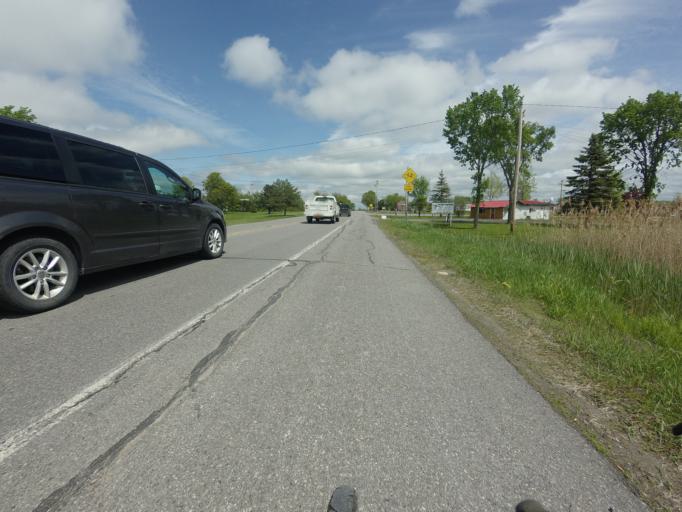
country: CA
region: Ontario
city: Cornwall
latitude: 44.9784
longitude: -74.6895
